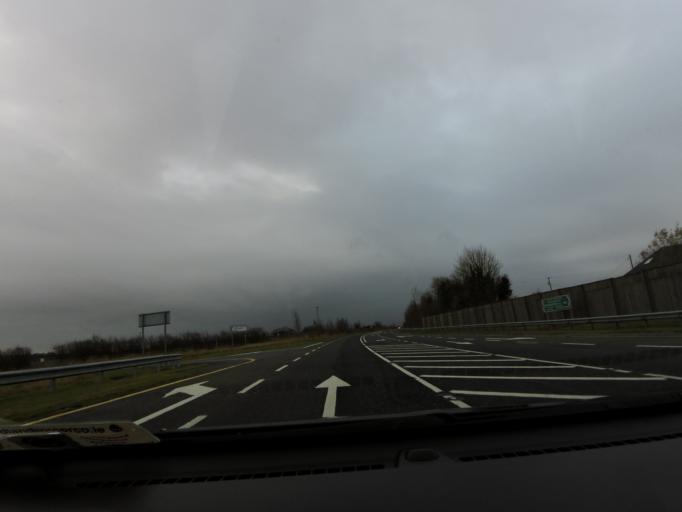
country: IE
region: Connaught
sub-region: County Galway
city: Loughrea
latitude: 53.2540
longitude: -8.5964
